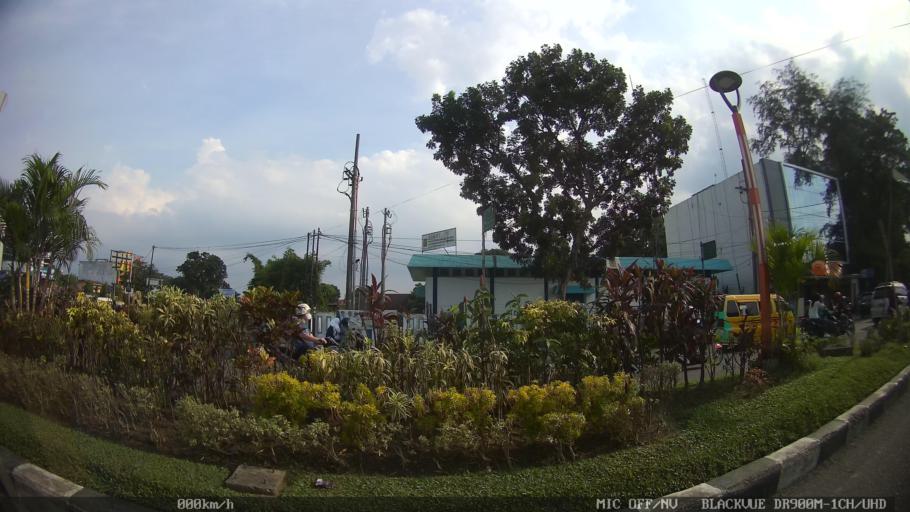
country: ID
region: North Sumatra
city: Binjai
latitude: 3.6105
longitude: 98.4944
